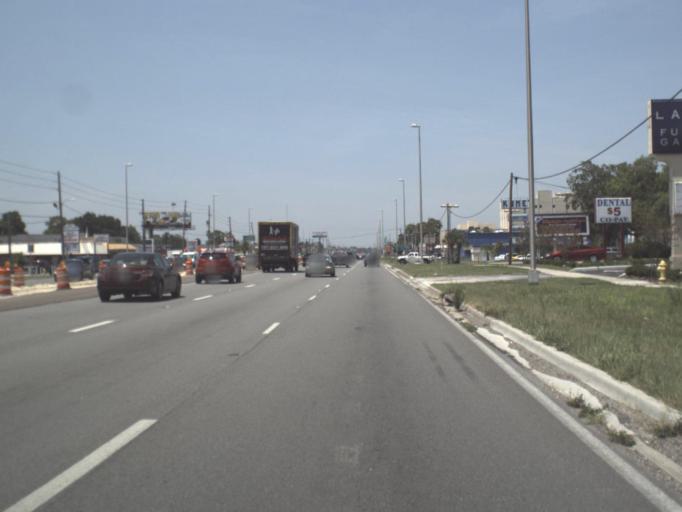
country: US
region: Florida
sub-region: Pasco County
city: New Port Richey
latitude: 28.2431
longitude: -82.7276
